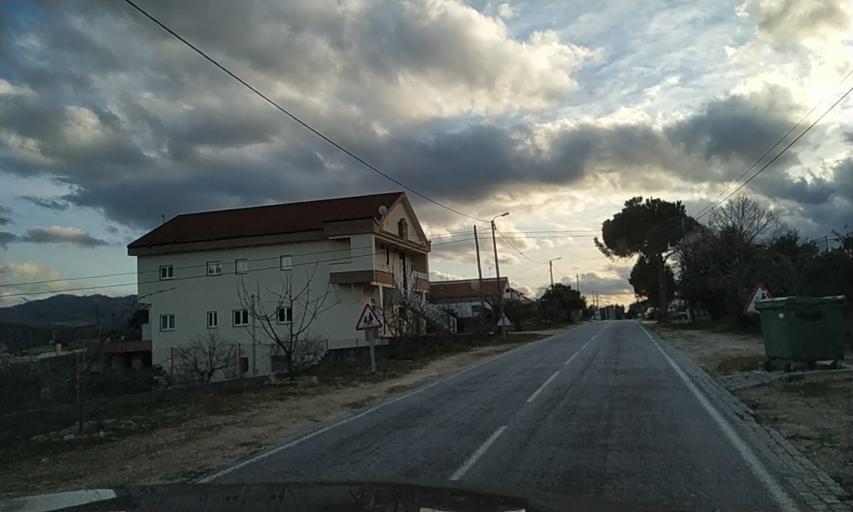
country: PT
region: Braganca
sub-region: Carrazeda de Ansiaes
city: Carrazeda de Anciaes
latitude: 41.2978
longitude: -7.3432
